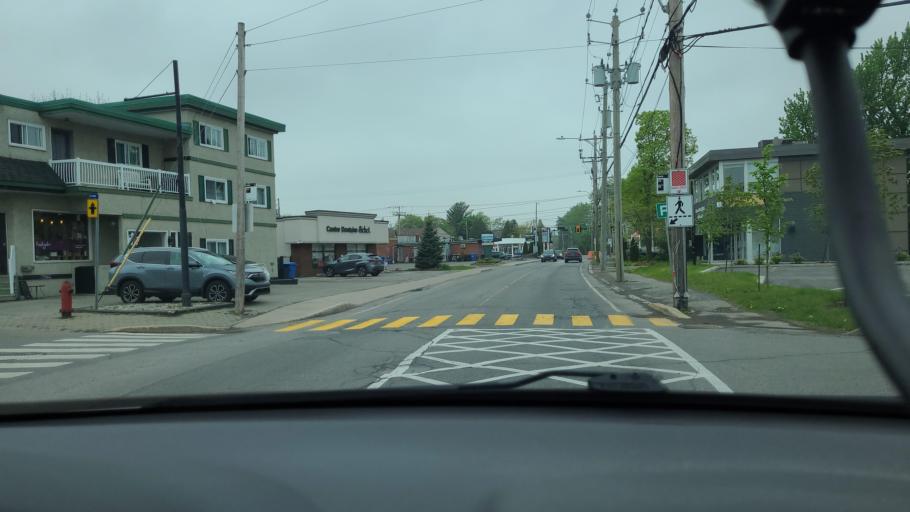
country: CA
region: Quebec
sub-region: Monteregie
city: L'Ile-Perrot
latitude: 45.3942
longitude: -73.9563
